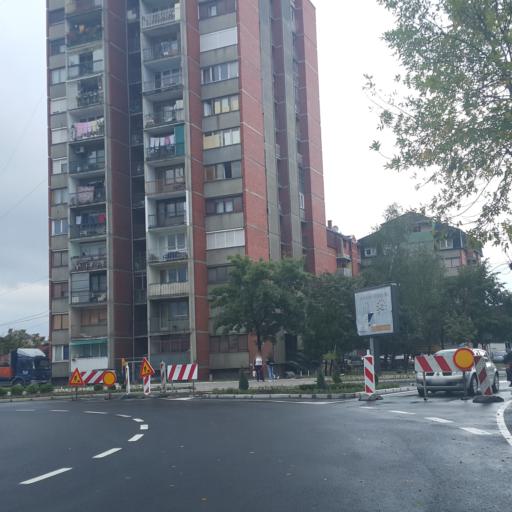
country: RS
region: Central Serbia
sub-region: Rasinski Okrug
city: Krusevac
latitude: 43.5709
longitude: 21.3384
